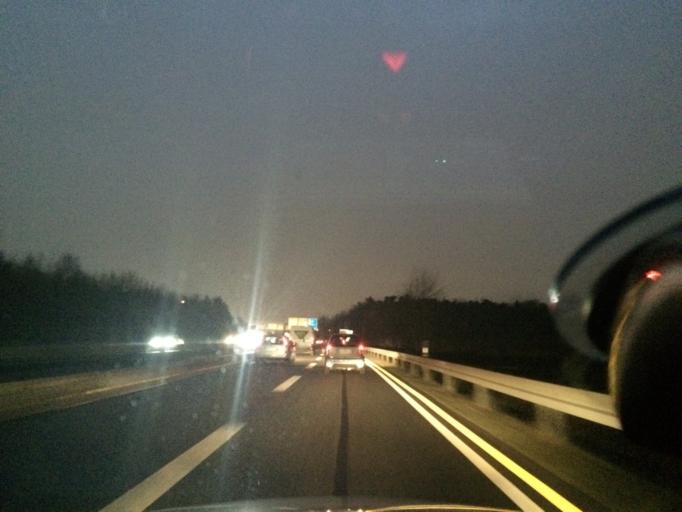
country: DE
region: Hesse
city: Kelsterbach
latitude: 50.0543
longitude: 8.5498
